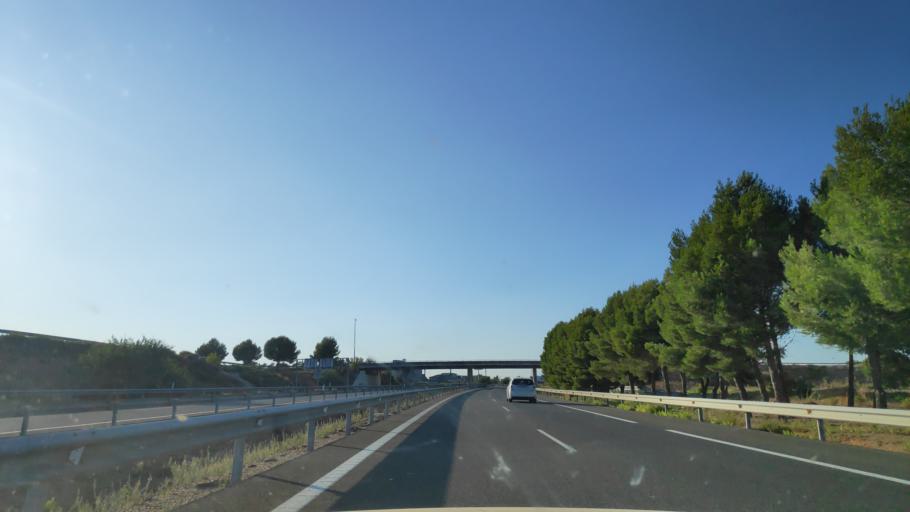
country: ES
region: Castille-La Mancha
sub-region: Provincia de Cuenca
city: Tarancon
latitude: 40.0035
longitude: -3.0261
